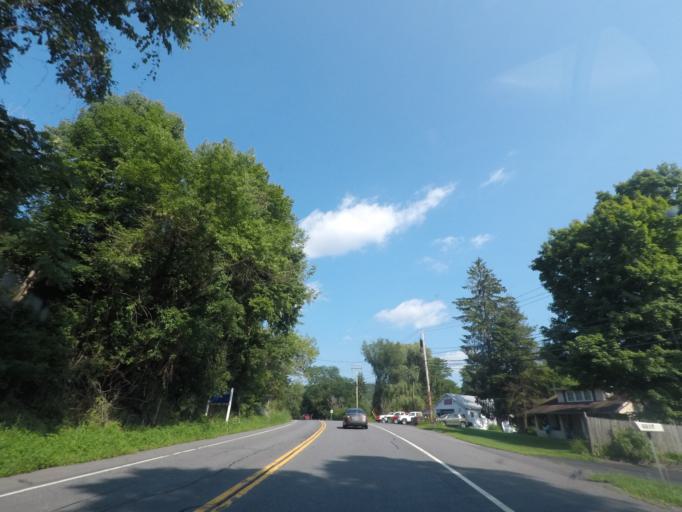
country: US
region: New York
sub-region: Rensselaer County
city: Nassau
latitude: 42.5123
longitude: -73.6034
